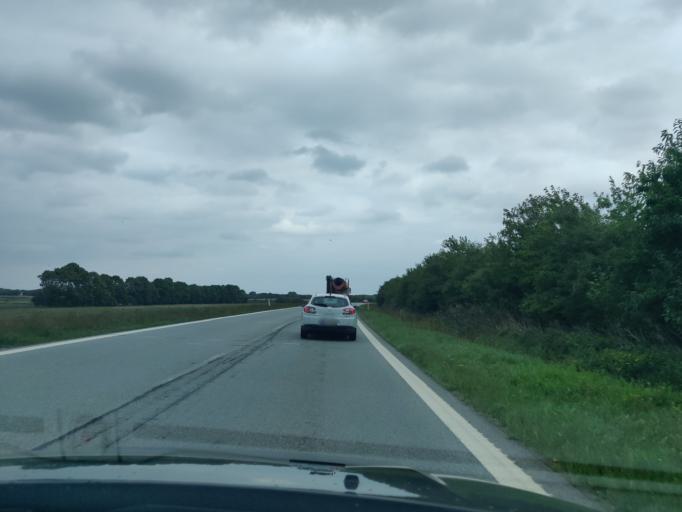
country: DK
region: North Denmark
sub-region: Alborg Kommune
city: Frejlev
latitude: 57.0124
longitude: 9.7482
